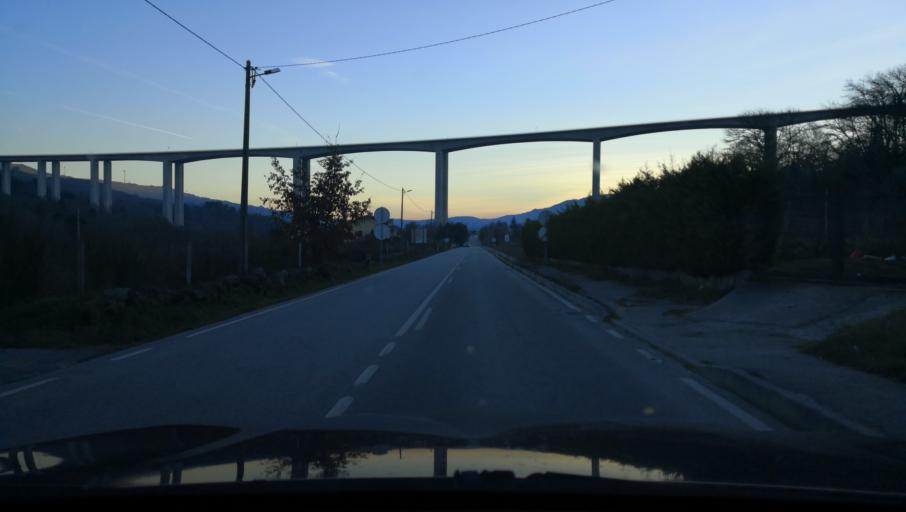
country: PT
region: Vila Real
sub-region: Vila Pouca de Aguiar
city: Vila Pouca de Aguiar
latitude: 41.4873
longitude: -7.6506
